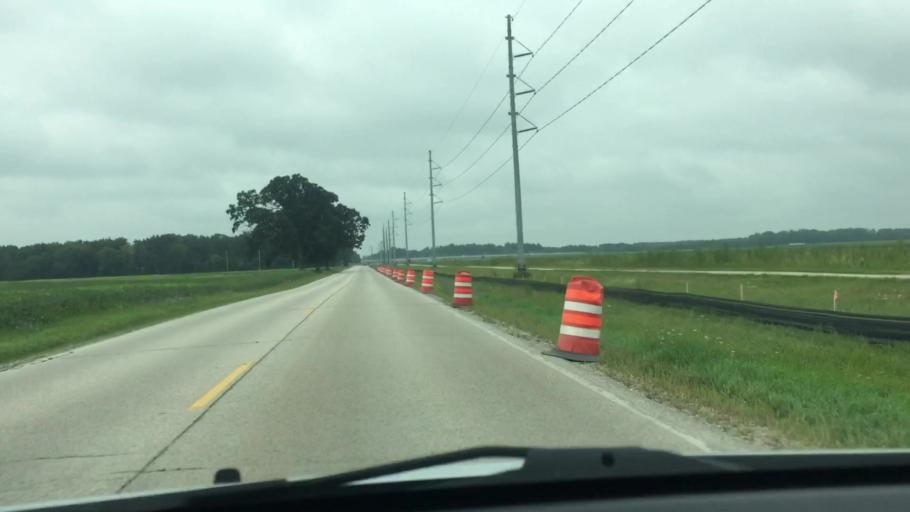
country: US
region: Wisconsin
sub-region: Waukesha County
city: Delafield
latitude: 43.0736
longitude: -88.4420
